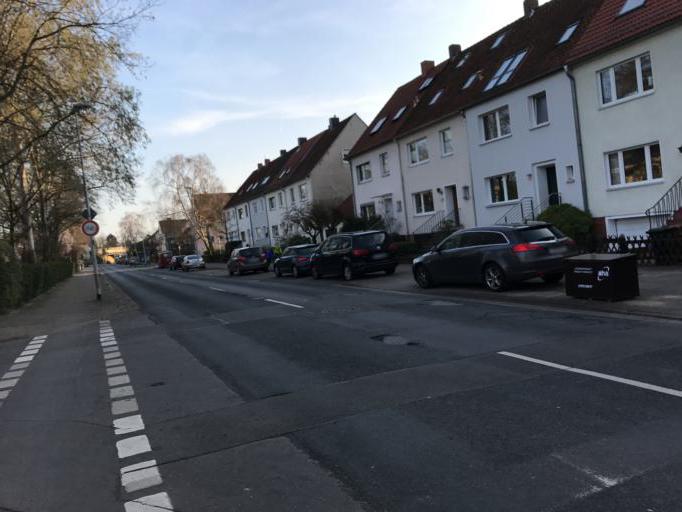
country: DE
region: Lower Saxony
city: Laatzen
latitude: 52.3516
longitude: 9.7818
